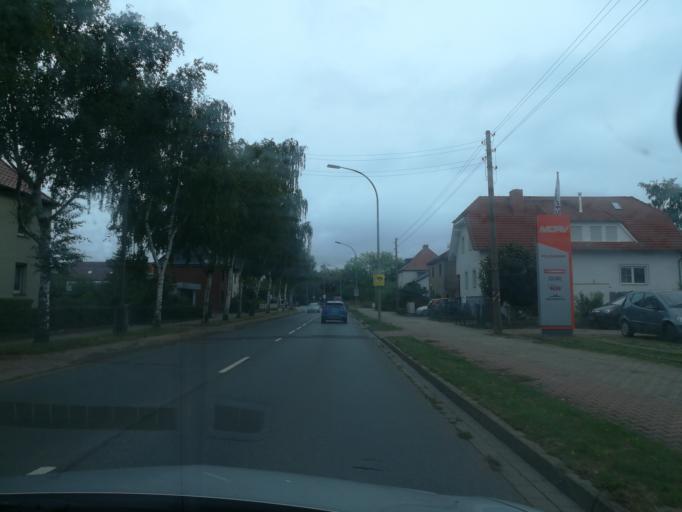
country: DE
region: Saxony-Anhalt
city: Diesdorf
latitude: 52.1557
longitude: 11.5762
